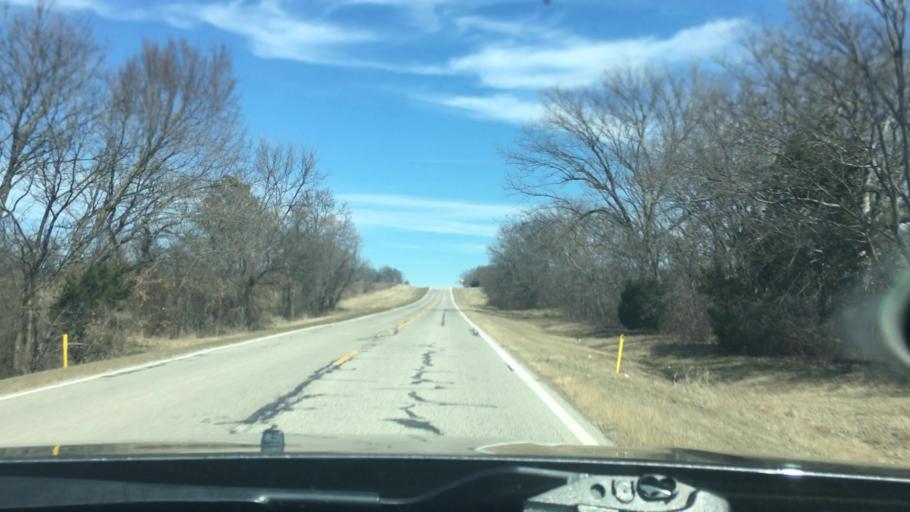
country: US
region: Oklahoma
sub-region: Carter County
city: Dickson
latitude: 34.3287
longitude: -96.9549
